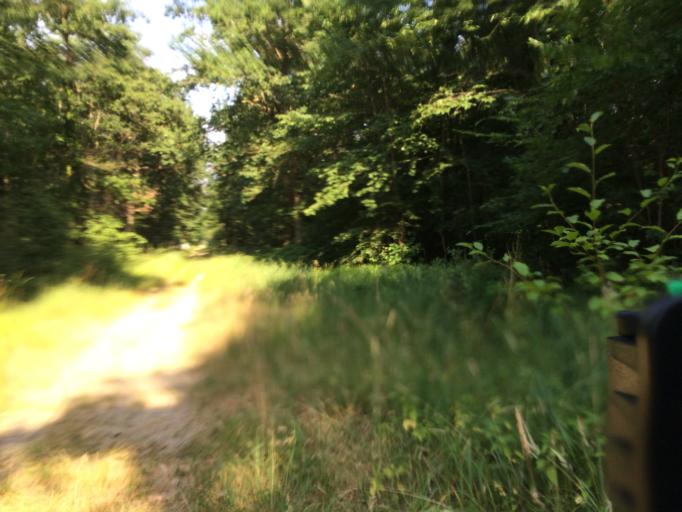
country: FR
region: Ile-de-France
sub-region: Departement de l'Essonne
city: Brunoy
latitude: 48.6672
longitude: 2.4832
